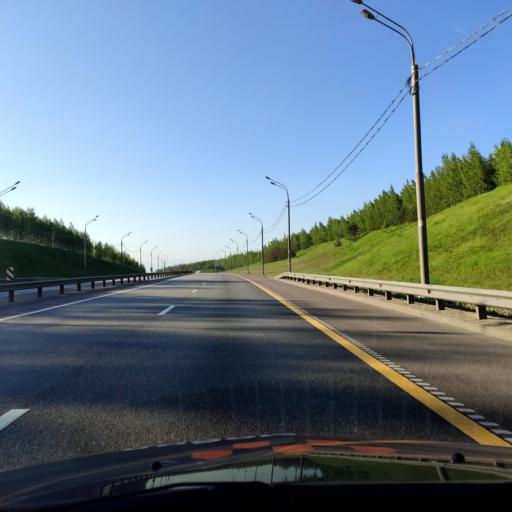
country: RU
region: Lipetsk
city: Zadonsk
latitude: 52.3911
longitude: 38.8642
